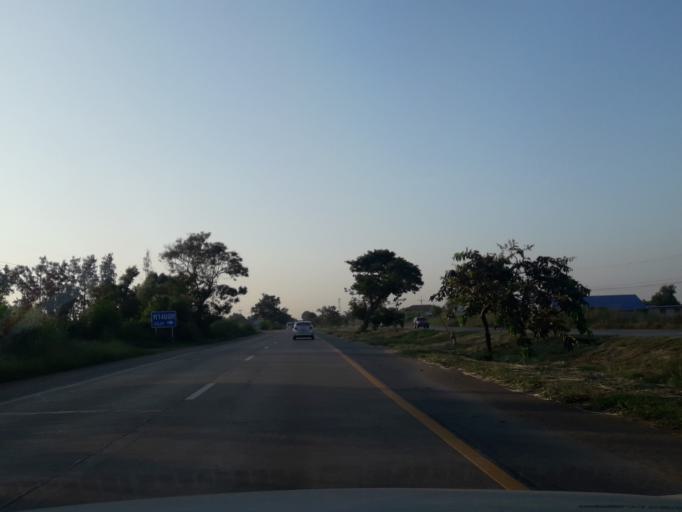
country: TH
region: Phra Nakhon Si Ayutthaya
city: Bang Pa-in
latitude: 14.2568
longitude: 100.5349
